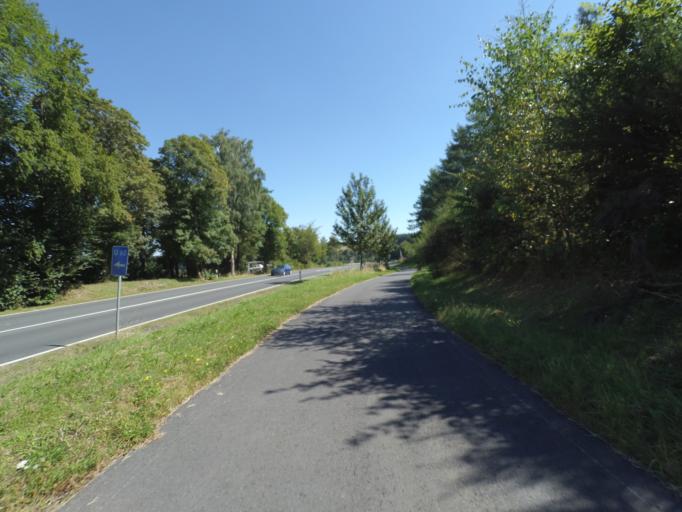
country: DE
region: Rheinland-Pfalz
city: Alflen
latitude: 50.1862
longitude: 7.0598
